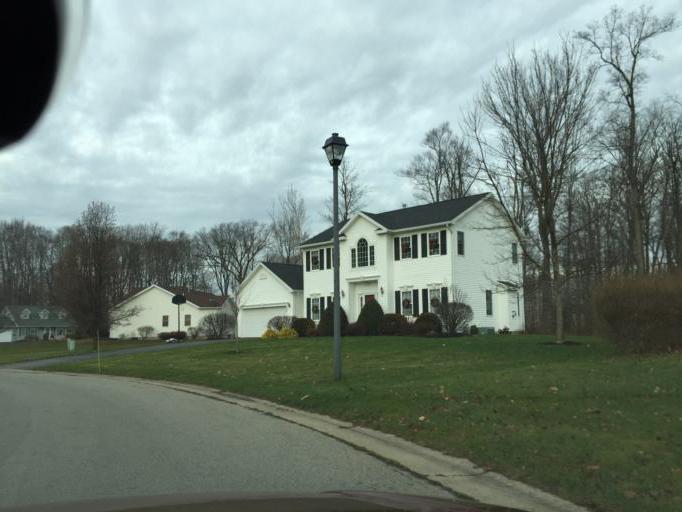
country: US
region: New York
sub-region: Monroe County
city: North Gates
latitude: 43.1117
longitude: -77.7231
